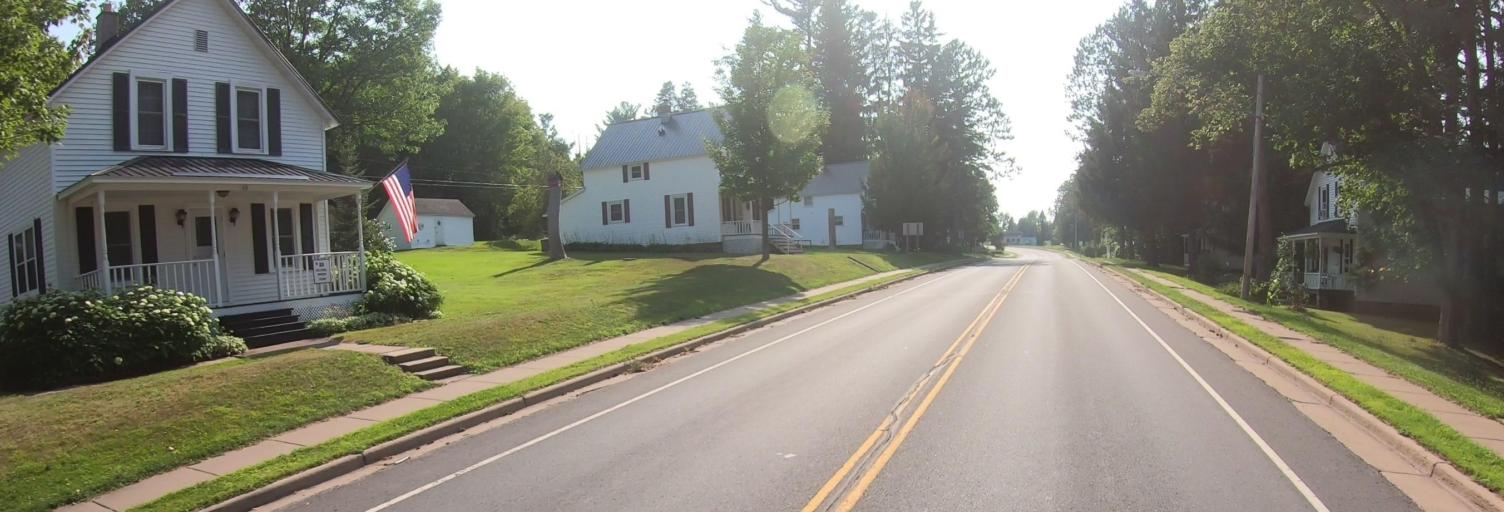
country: US
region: Wisconsin
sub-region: Iron County
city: Hurley
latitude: 46.4283
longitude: -90.2438
